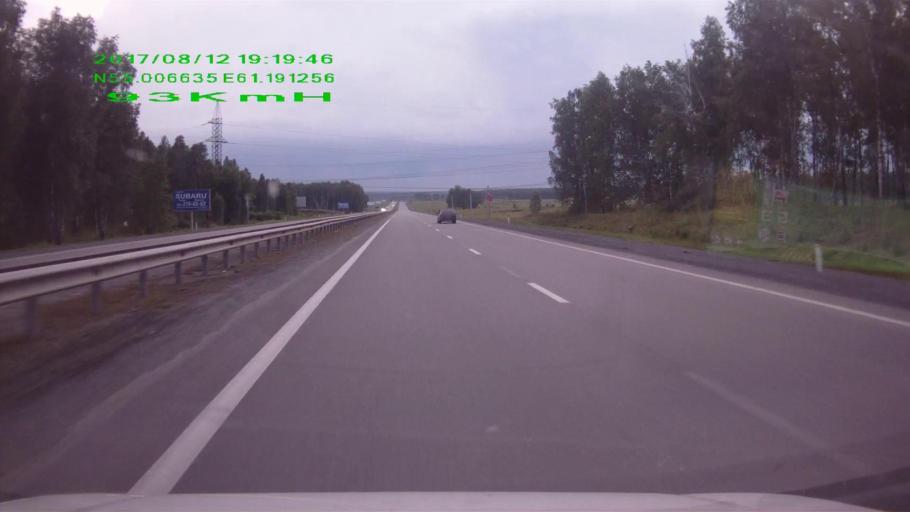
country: RU
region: Chelyabinsk
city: Sargazy
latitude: 55.0064
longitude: 61.1875
